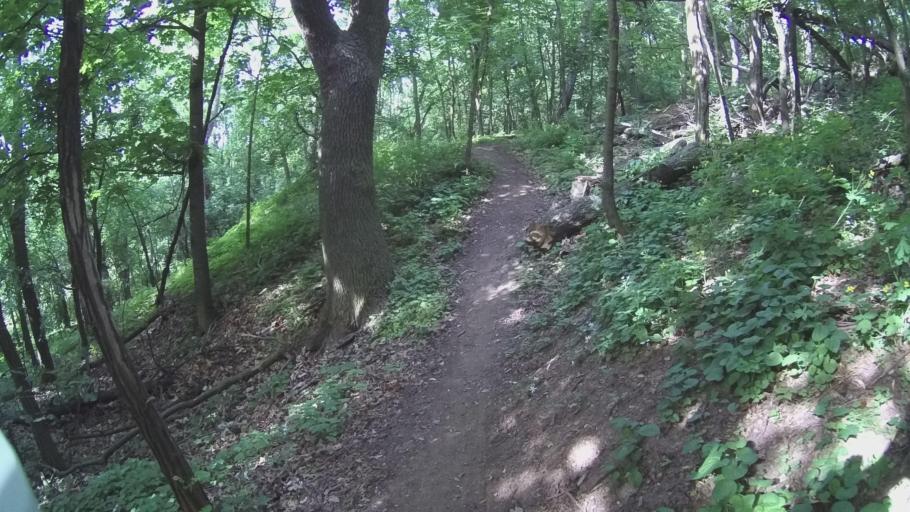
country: CZ
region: Praha
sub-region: Praha 19
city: Kbely
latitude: 50.1651
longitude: 14.5469
